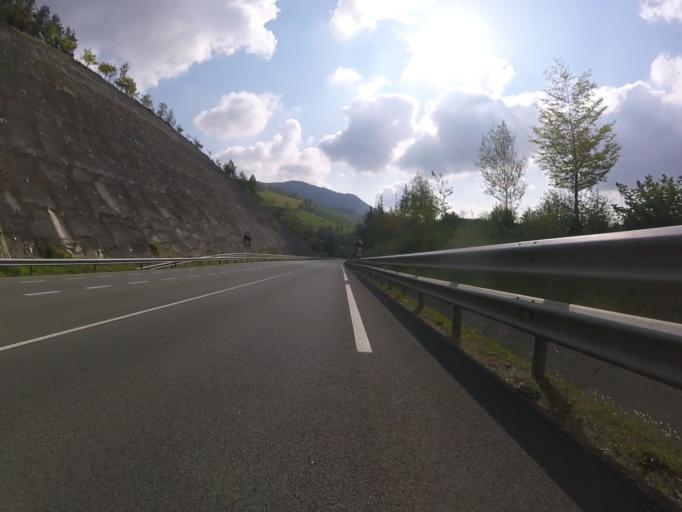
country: ES
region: Basque Country
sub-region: Provincia de Guipuzcoa
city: Azkoitia
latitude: 43.2010
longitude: -2.3492
